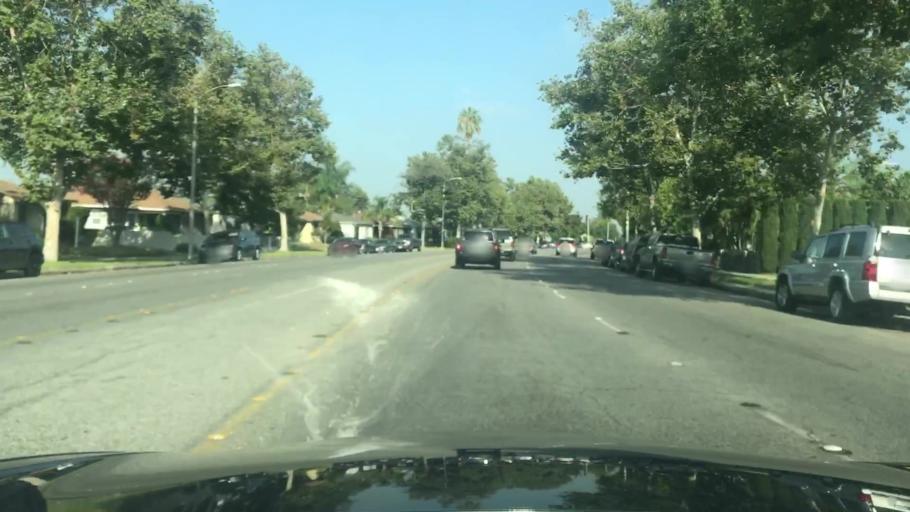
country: US
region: California
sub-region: Los Angeles County
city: Bellflower
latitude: 33.9021
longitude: -118.1263
